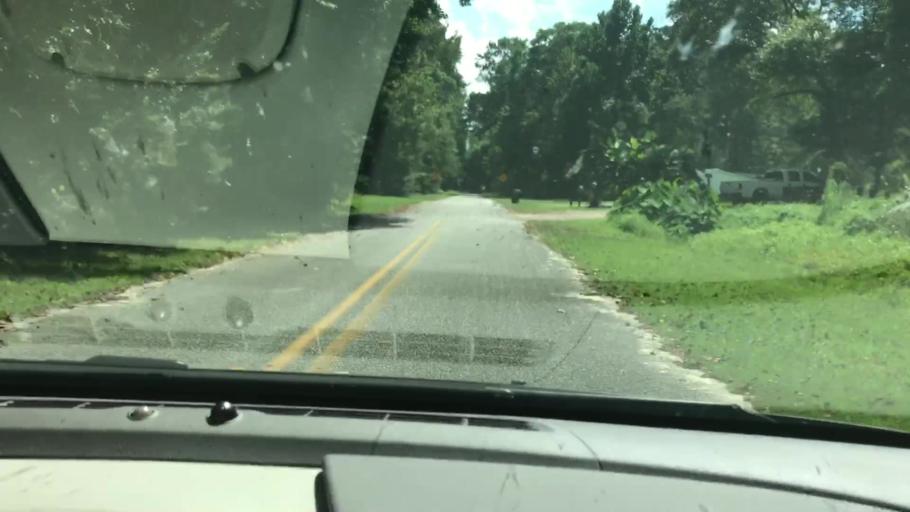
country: US
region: Georgia
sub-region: Clay County
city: Fort Gaines
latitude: 31.7327
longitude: -85.0928
